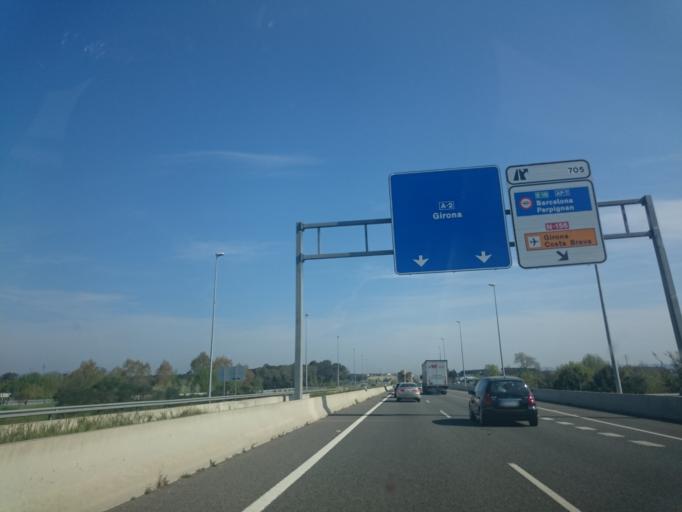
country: ES
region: Catalonia
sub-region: Provincia de Girona
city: Riudellots de la Selva
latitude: 41.8831
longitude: 2.7815
